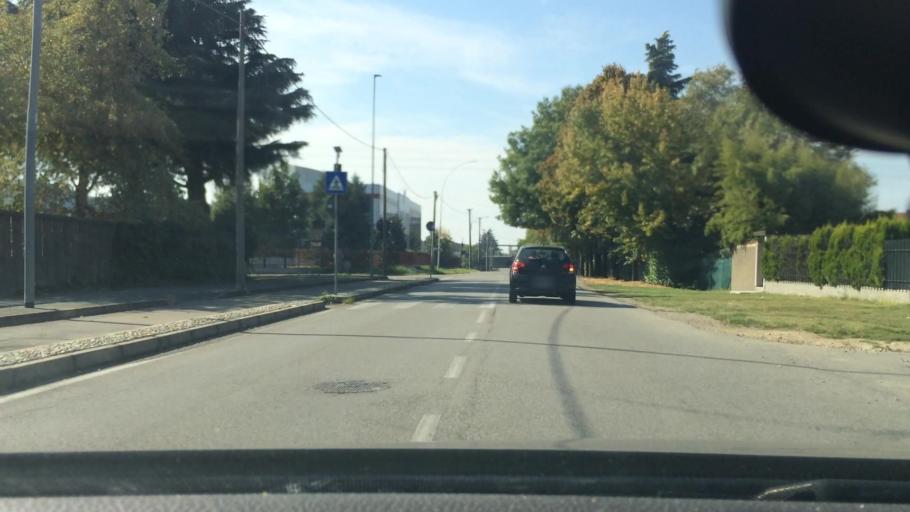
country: IT
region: Lombardy
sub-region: Citta metropolitana di Milano
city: Cerro Maggiore
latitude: 45.5993
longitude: 8.9609
